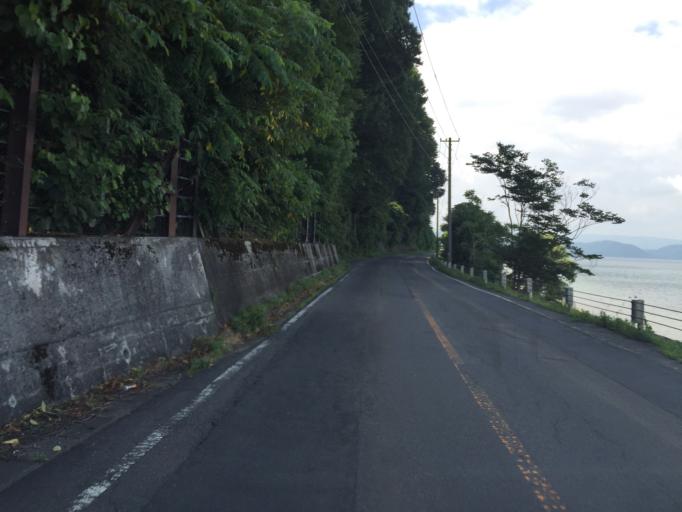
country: JP
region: Fukushima
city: Inawashiro
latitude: 37.4587
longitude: 140.1532
